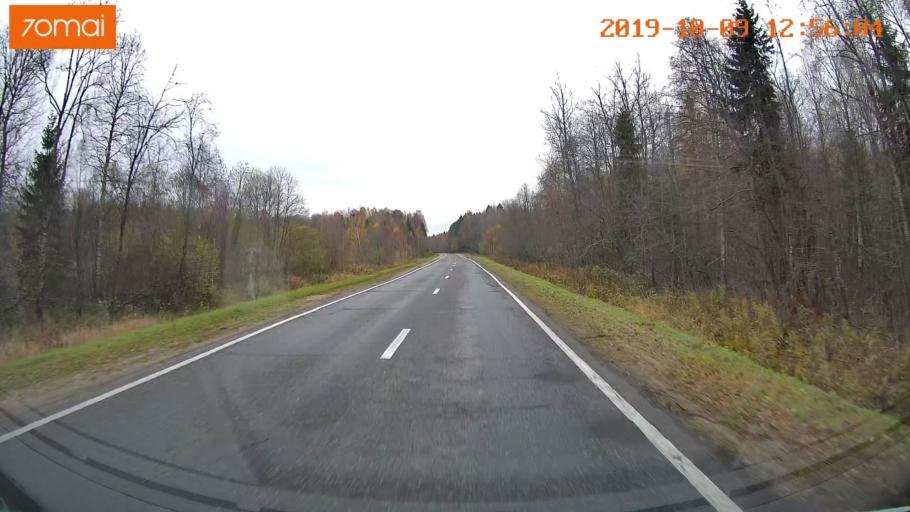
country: RU
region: Jaroslavl
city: Prechistoye
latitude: 58.3960
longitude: 40.4088
